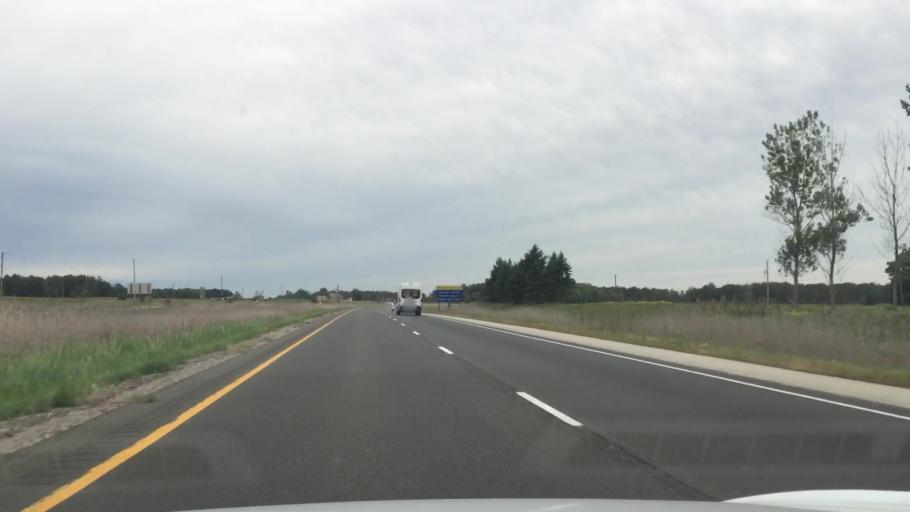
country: CA
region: Ontario
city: Delaware
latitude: 42.8854
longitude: -81.3314
